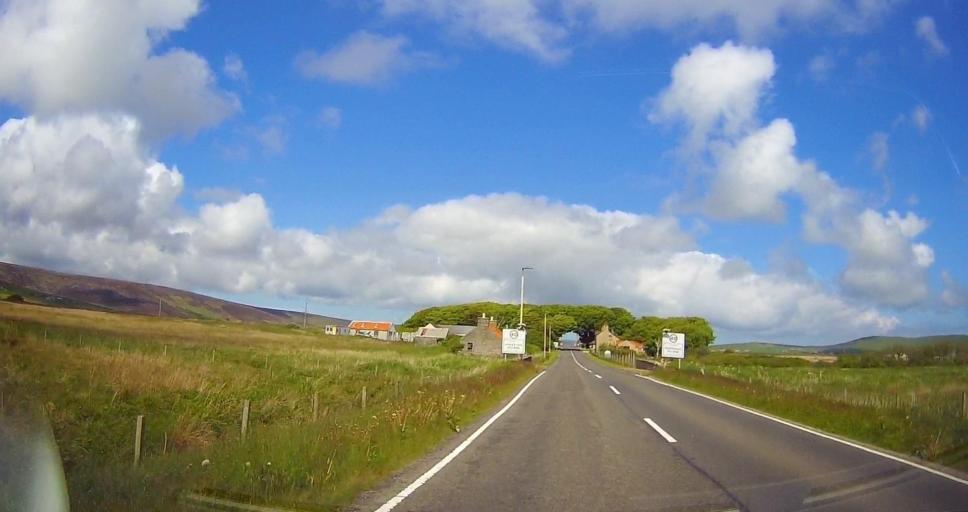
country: GB
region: Scotland
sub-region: Orkney Islands
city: Orkney
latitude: 59.0446
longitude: -3.0844
